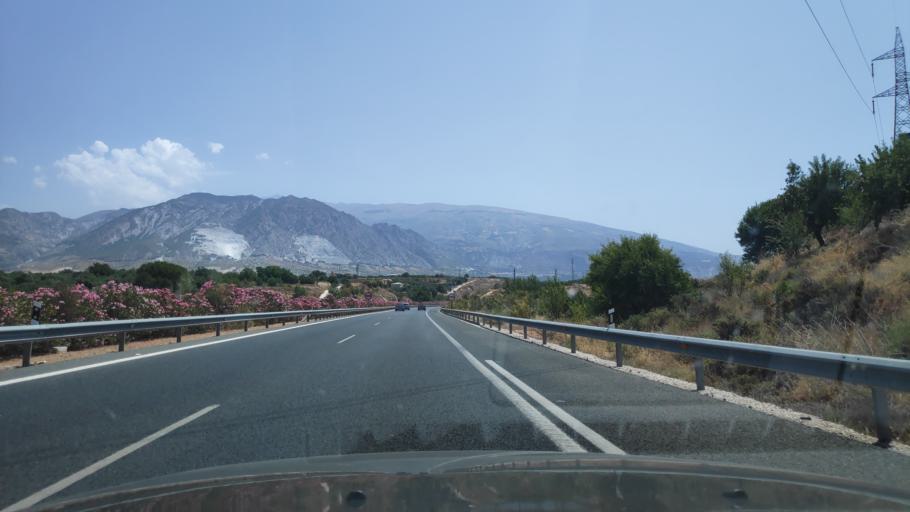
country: ES
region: Andalusia
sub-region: Provincia de Granada
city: Durcal
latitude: 36.9877
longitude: -3.5990
